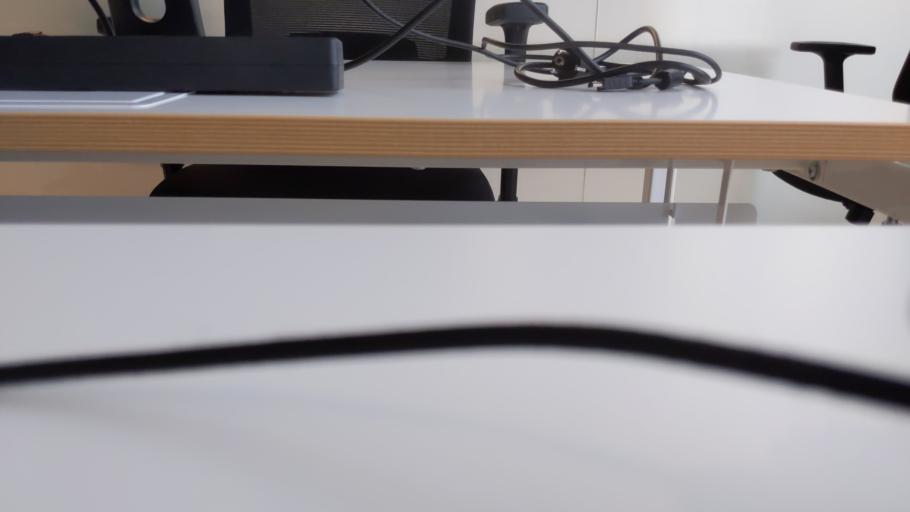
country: RU
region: Moskovskaya
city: Rogachevo
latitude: 56.4159
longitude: 37.0321
